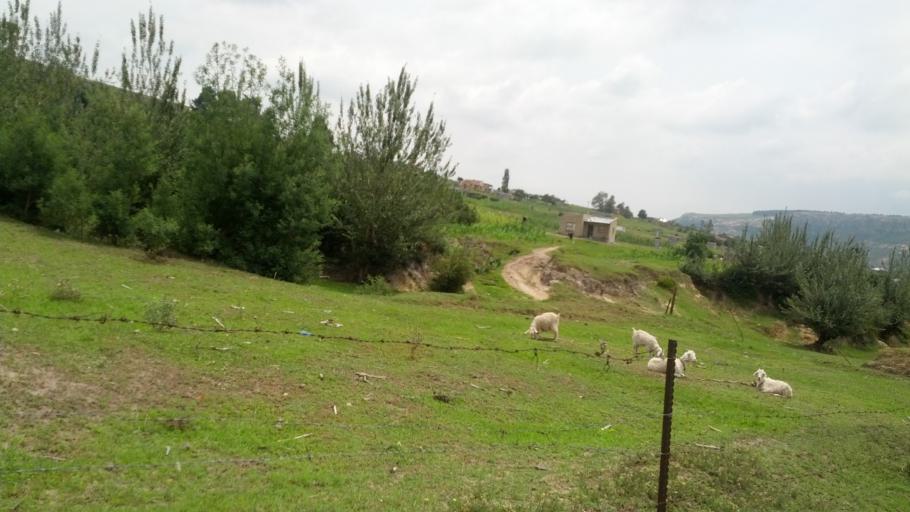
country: LS
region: Leribe
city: Leribe
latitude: -29.0316
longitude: 28.0202
